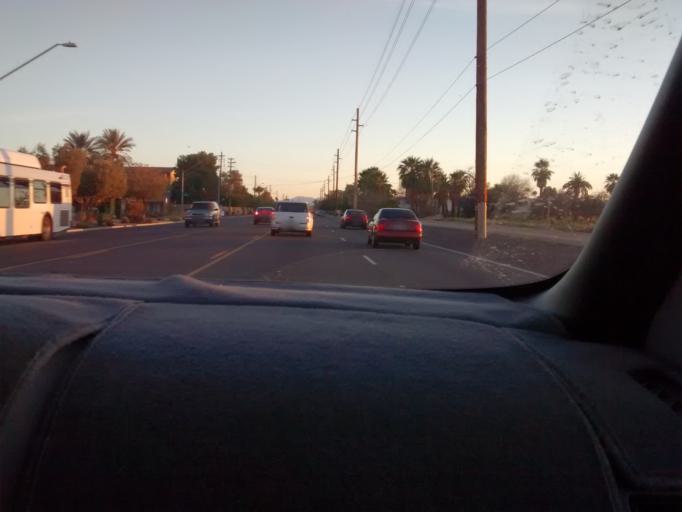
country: US
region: Arizona
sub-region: Maricopa County
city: Glendale
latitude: 33.5646
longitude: -112.2030
